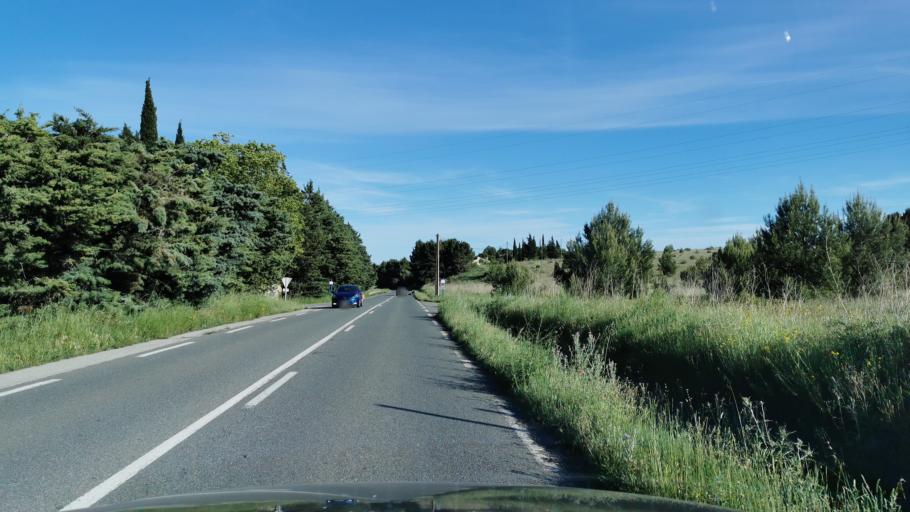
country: FR
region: Languedoc-Roussillon
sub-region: Departement de l'Aude
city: Moussan
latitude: 43.2047
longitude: 2.9629
